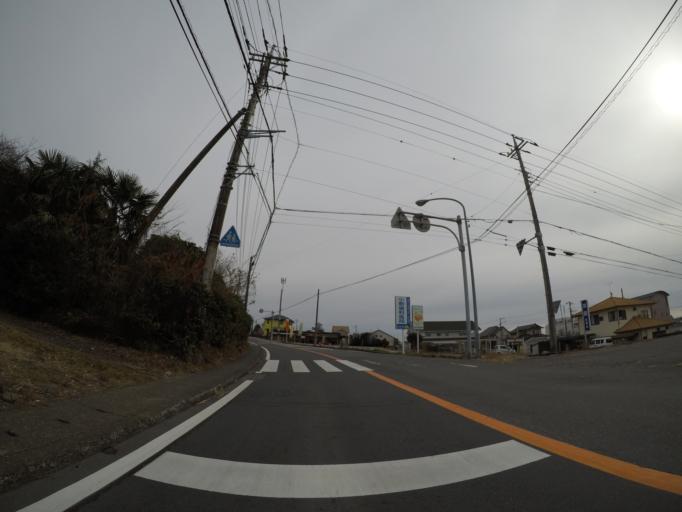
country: JP
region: Shizuoka
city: Fuji
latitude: 35.2114
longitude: 138.6834
